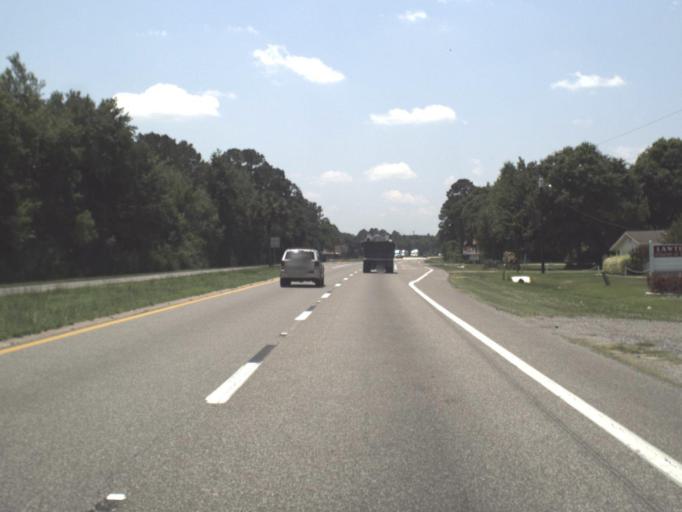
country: US
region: Florida
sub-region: Bradford County
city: Starke
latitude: 30.0370
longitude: -82.0747
